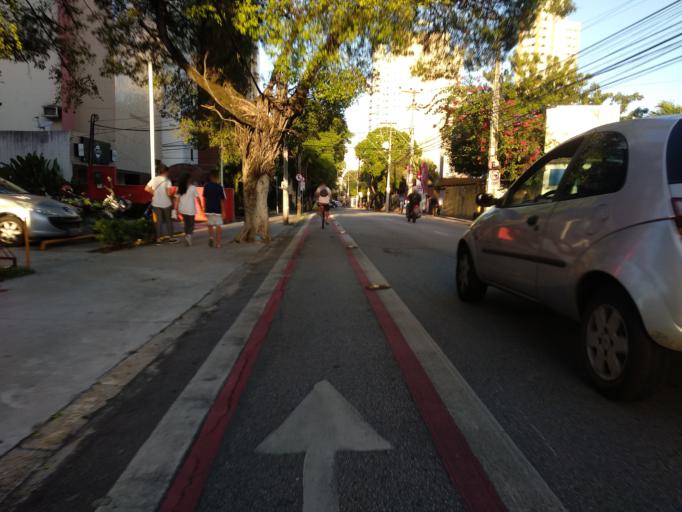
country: BR
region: Ceara
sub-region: Fortaleza
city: Fortaleza
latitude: -3.7316
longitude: -38.5125
